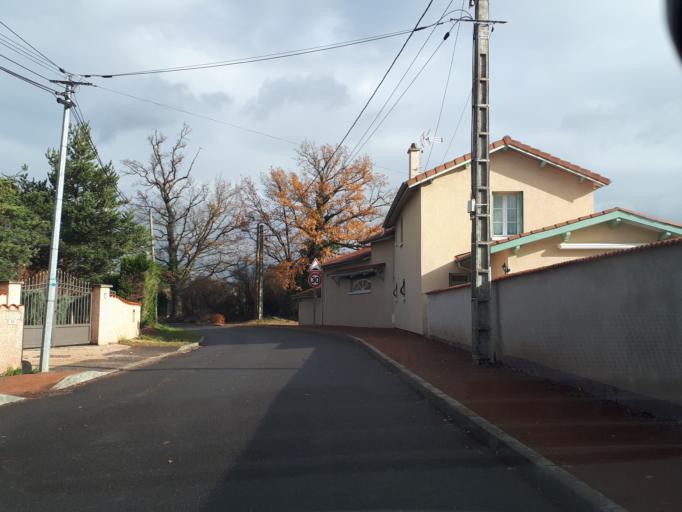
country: FR
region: Rhone-Alpes
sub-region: Departement de la Loire
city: Cuzieu
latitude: 45.6135
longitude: 4.2646
